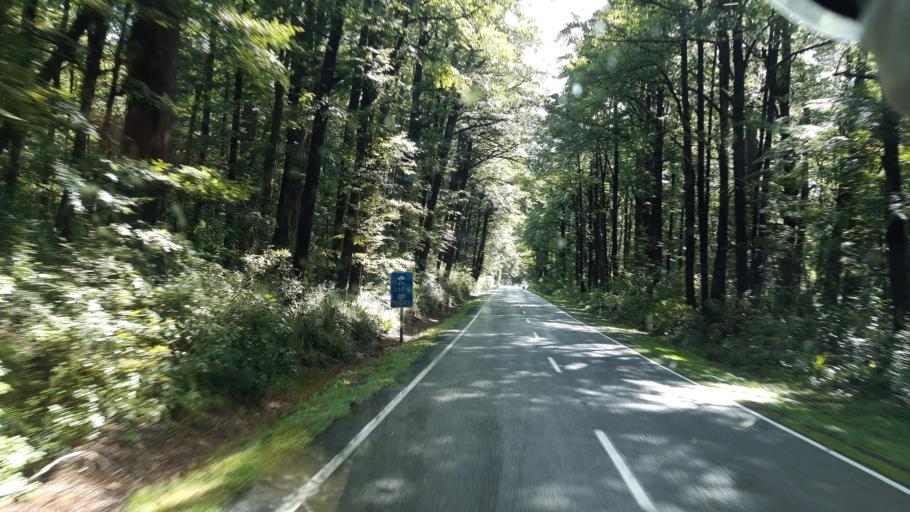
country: NZ
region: Canterbury
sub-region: Hurunui District
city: Amberley
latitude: -42.3802
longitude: 172.2818
